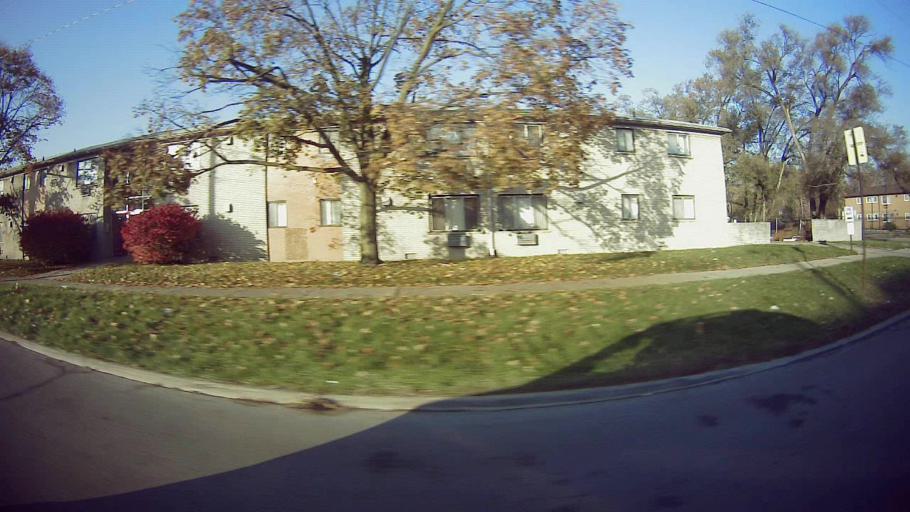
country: US
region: Michigan
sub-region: Oakland County
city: Oak Park
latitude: 42.4175
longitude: -83.1994
